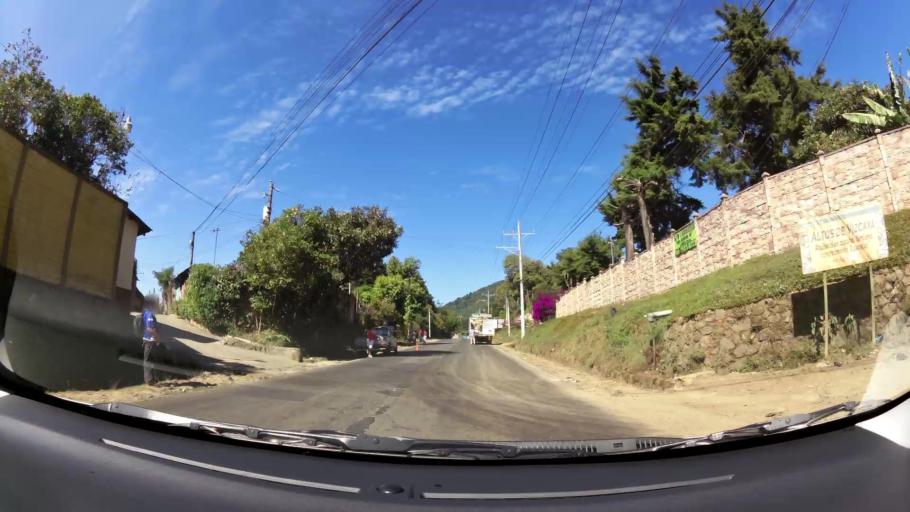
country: SV
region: Ahuachapan
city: Concepcion de Ataco
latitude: 13.8637
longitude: -89.7985
